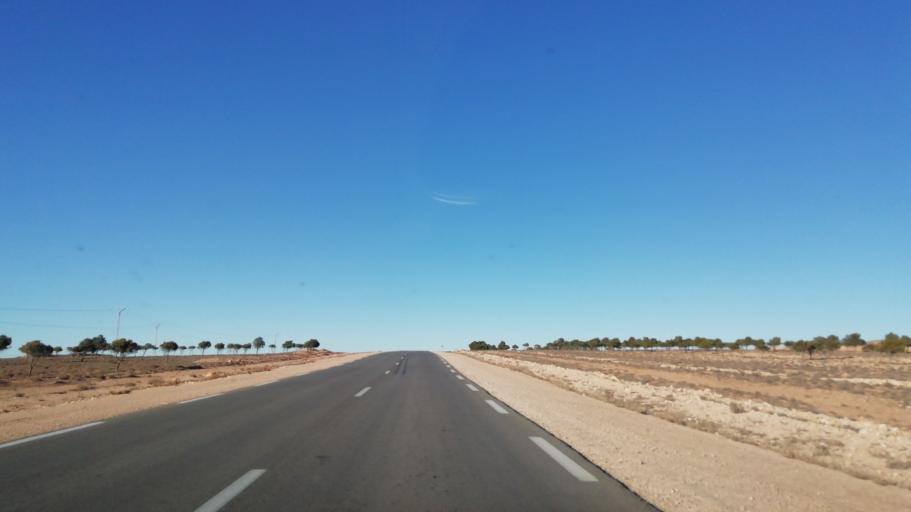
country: DZ
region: Tlemcen
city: Sebdou
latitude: 34.2566
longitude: -1.2577
